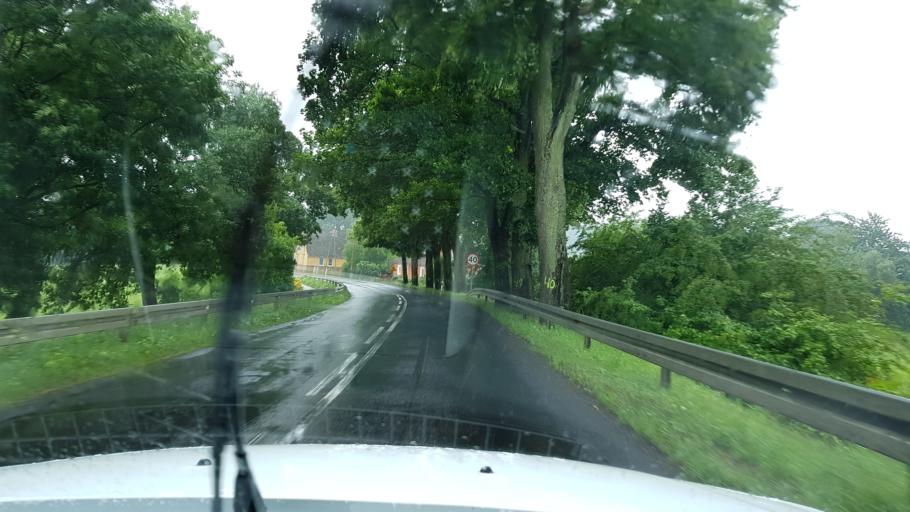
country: PL
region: West Pomeranian Voivodeship
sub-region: Powiat goleniowski
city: Nowogard
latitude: 53.5956
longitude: 15.1524
